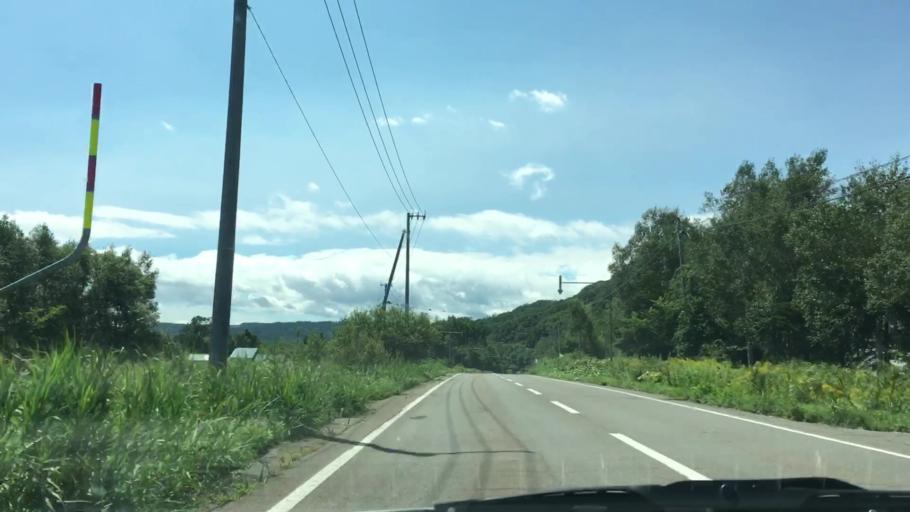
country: JP
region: Hokkaido
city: Otofuke
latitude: 43.2575
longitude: 143.5714
